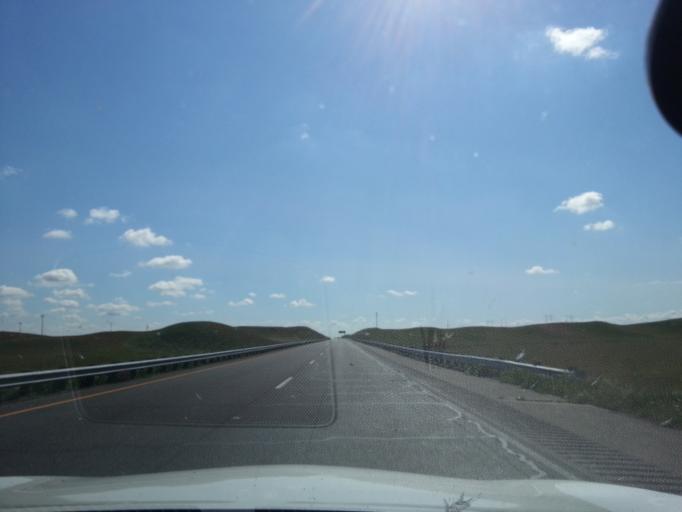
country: US
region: California
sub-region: Fresno County
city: Coalinga
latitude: 36.3144
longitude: -120.2867
